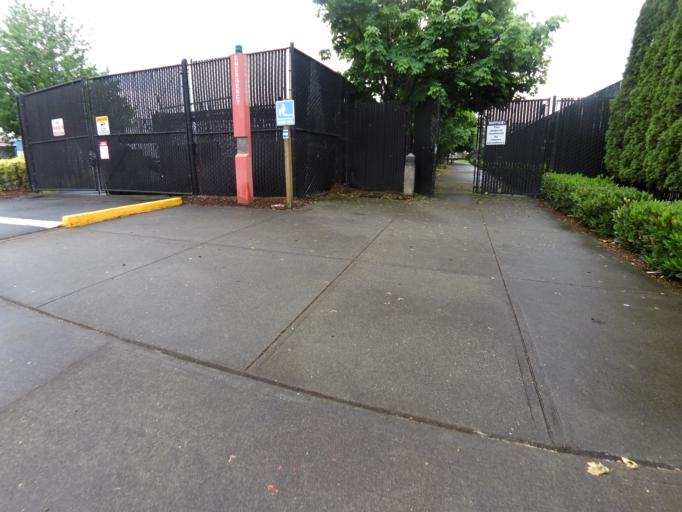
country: US
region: Washington
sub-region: King County
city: Seattle
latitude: 47.6594
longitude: -122.3698
